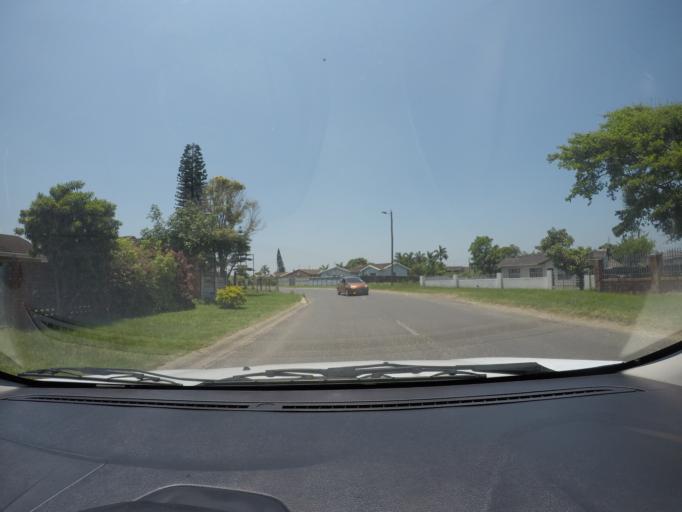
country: ZA
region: KwaZulu-Natal
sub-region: uThungulu District Municipality
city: eSikhawini
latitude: -28.8869
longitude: 31.8920
